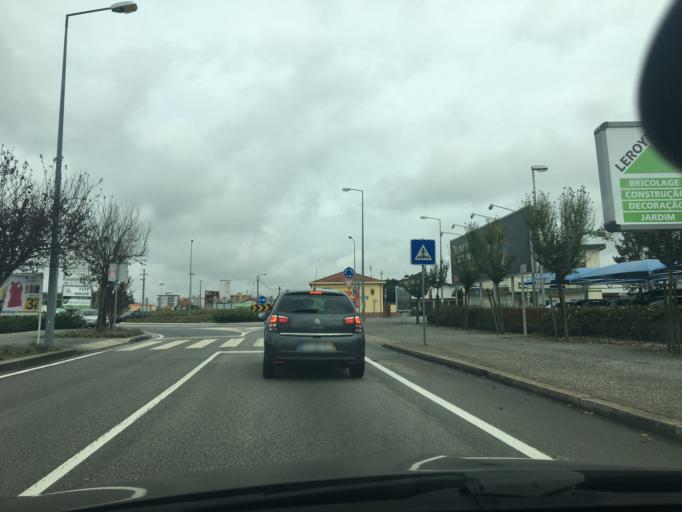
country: PT
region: Porto
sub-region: Maia
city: Anta
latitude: 41.2542
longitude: -8.6166
